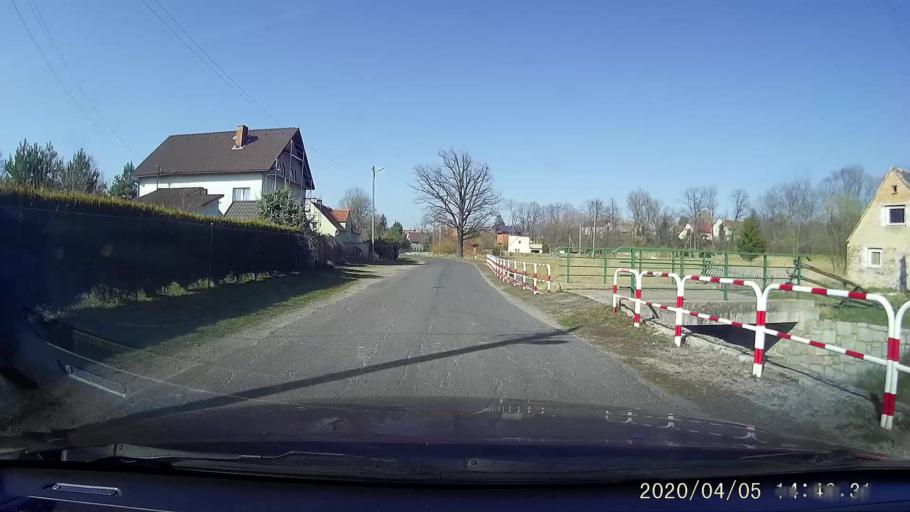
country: PL
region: Lower Silesian Voivodeship
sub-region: Powiat zgorzelecki
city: Sulikow
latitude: 51.0583
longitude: 15.1094
